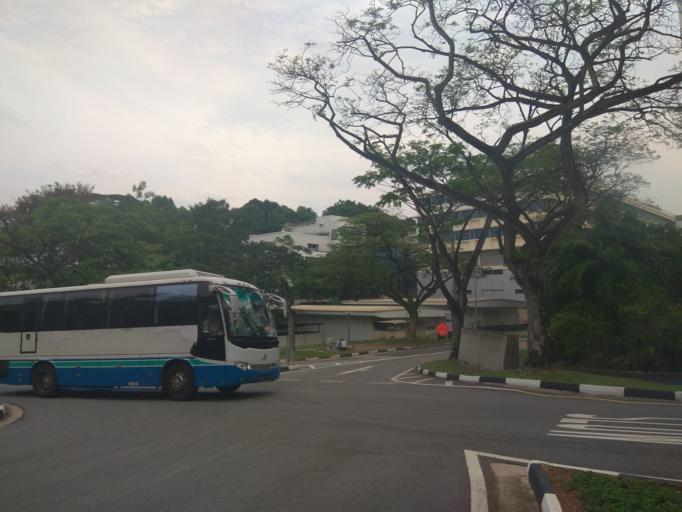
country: MY
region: Johor
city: Johor Bahru
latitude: 1.3487
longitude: 103.6819
